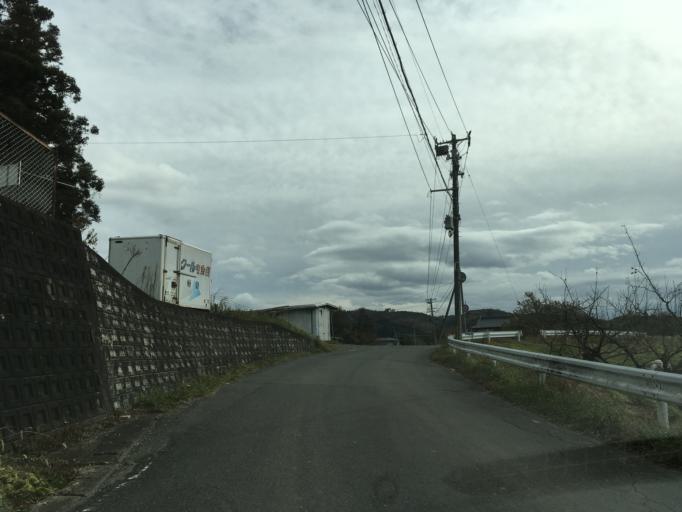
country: JP
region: Iwate
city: Ichinoseki
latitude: 38.7610
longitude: 141.2762
